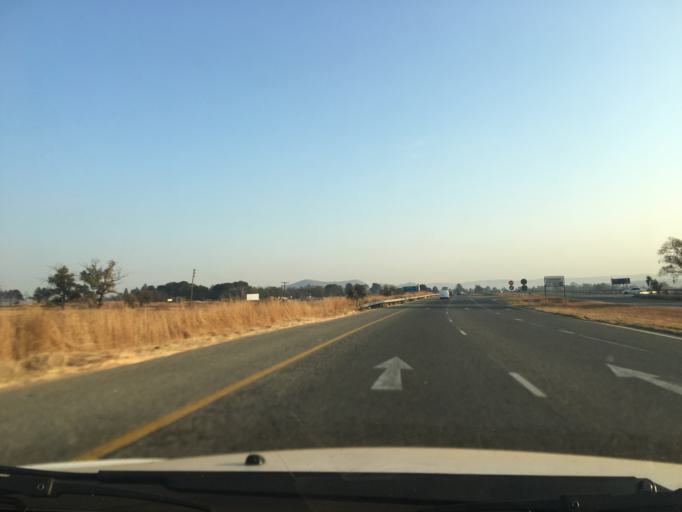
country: ZA
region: Gauteng
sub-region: West Rand District Municipality
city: Muldersdriseloop
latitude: -26.0231
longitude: 27.8614
